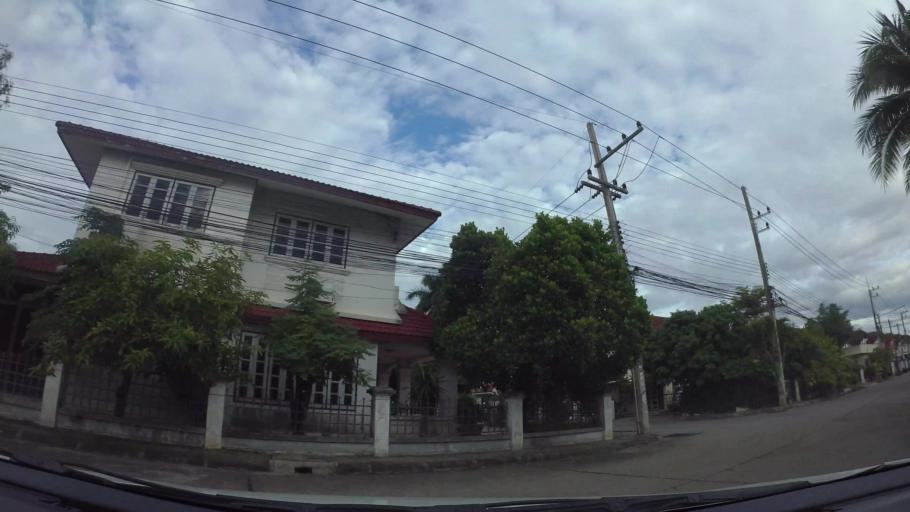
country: TH
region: Chiang Mai
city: Saraphi
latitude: 18.7400
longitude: 99.0315
